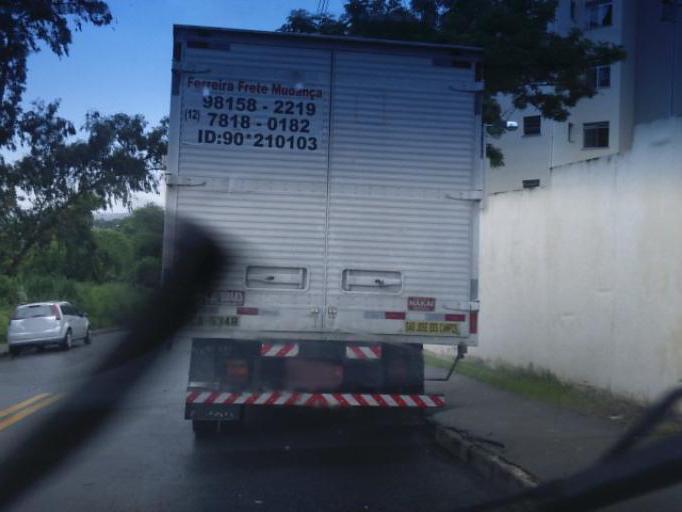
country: BR
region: Sao Paulo
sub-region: Sao Jose Dos Campos
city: Sao Jose dos Campos
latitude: -23.1991
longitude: -45.8638
